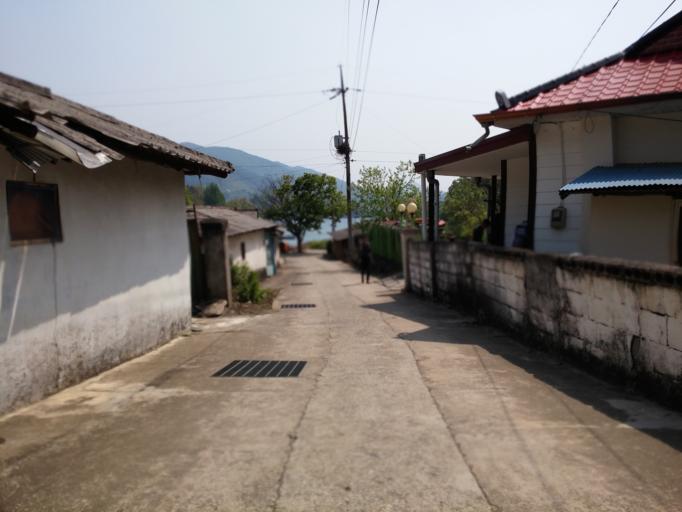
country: KR
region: Chungcheongbuk-do
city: Okcheon
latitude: 36.3745
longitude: 127.6066
